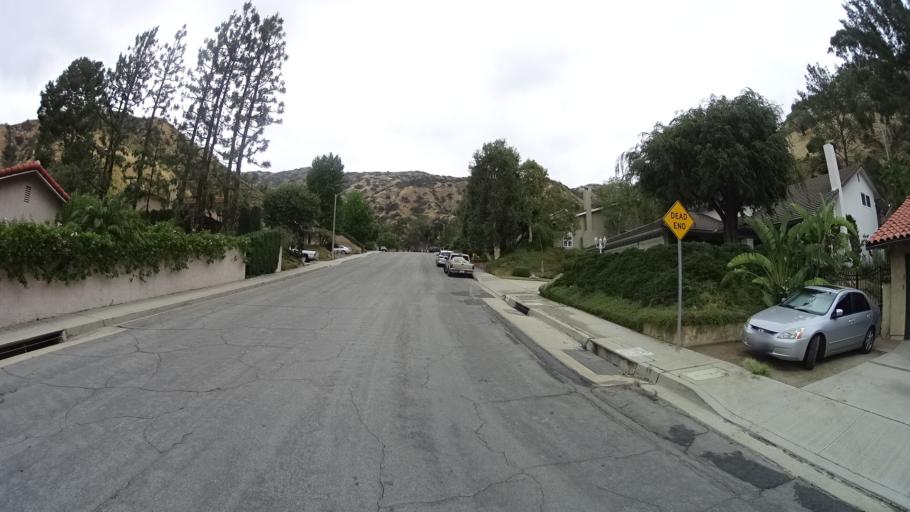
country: US
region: California
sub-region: Los Angeles County
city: Burbank
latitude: 34.2133
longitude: -118.3239
